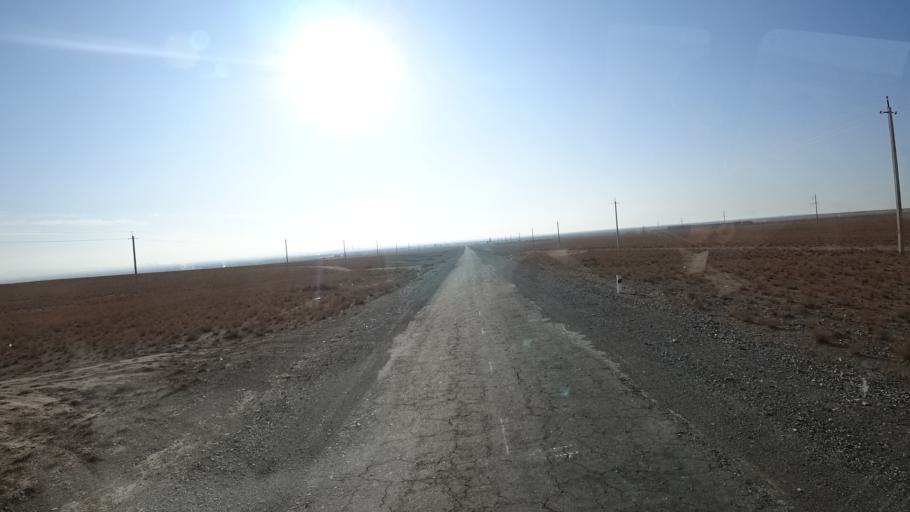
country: UZ
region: Navoiy
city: Beshrabot
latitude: 40.2293
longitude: 65.4070
